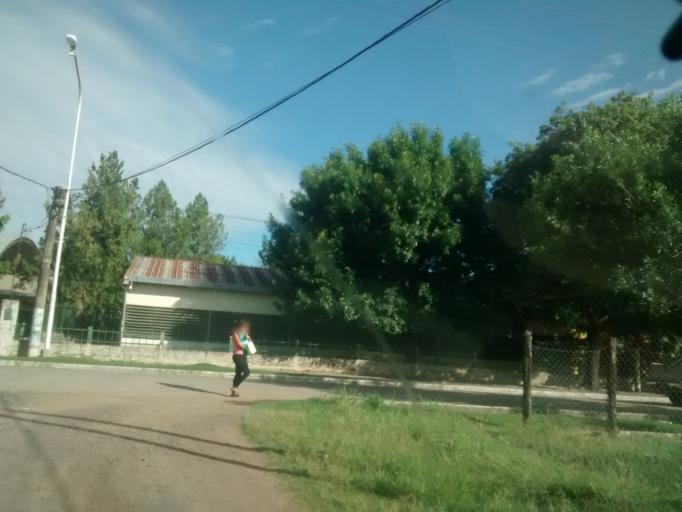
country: AR
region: Chaco
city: Puerto Tirol
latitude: -27.3744
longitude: -59.0912
